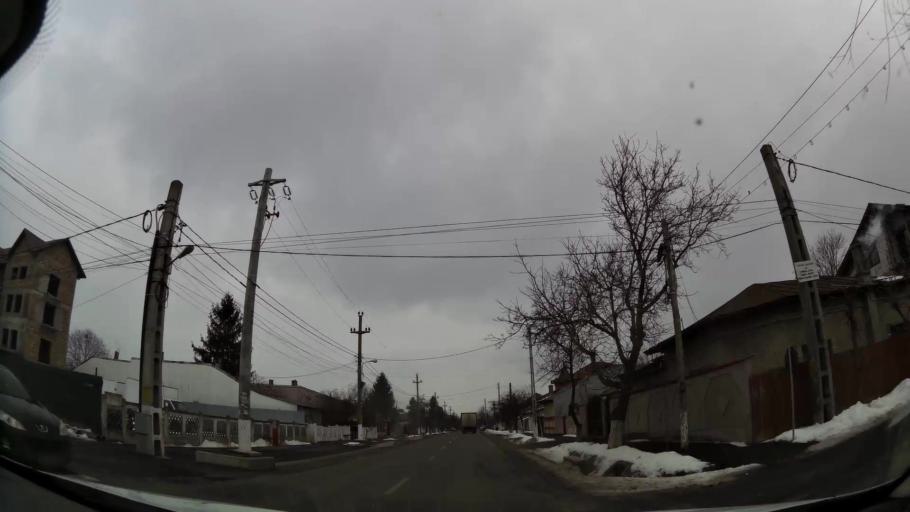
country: RO
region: Ilfov
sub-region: Comuna Afumati
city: Afumati
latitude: 44.5258
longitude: 26.2454
